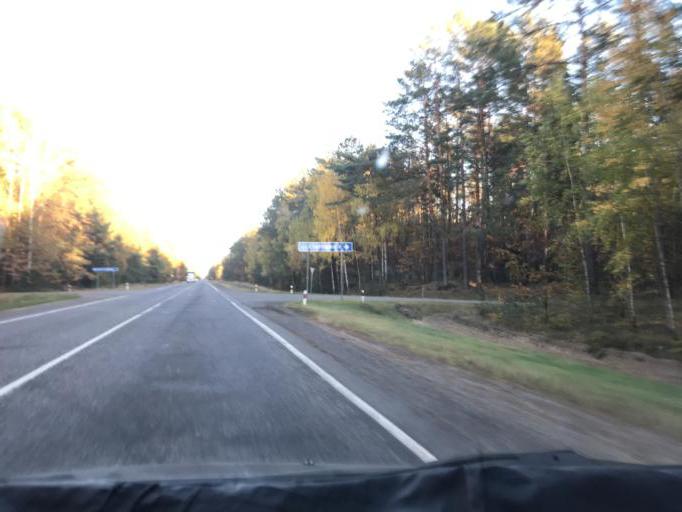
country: BY
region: Gomel
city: Pyetrykaw
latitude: 52.2748
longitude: 28.1946
